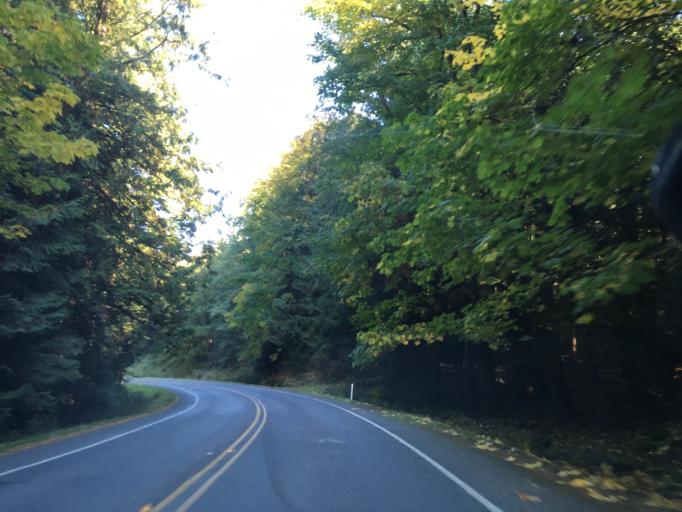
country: US
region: Washington
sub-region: San Juan County
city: Friday Harbor
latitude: 48.6200
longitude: -122.9438
